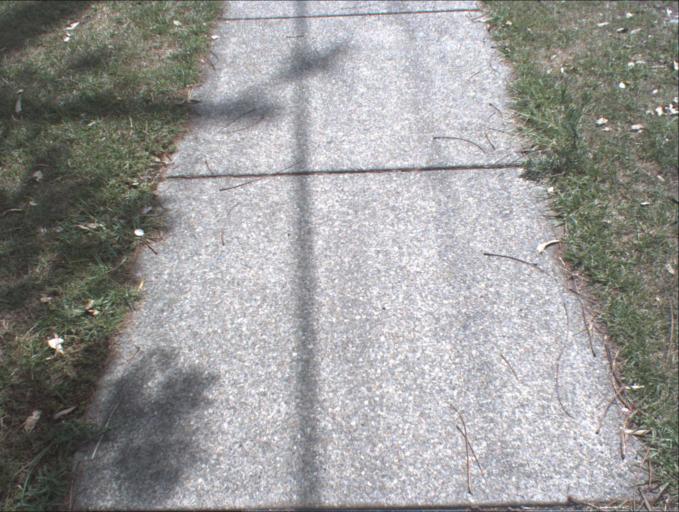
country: AU
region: Queensland
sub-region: Logan
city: Windaroo
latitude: -27.7224
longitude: 153.1929
